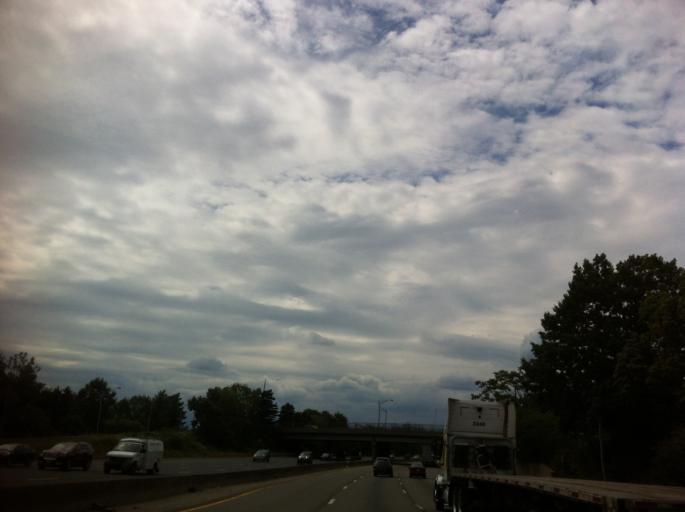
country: US
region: New Jersey
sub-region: Passaic County
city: Paterson
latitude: 40.9089
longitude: -74.1777
